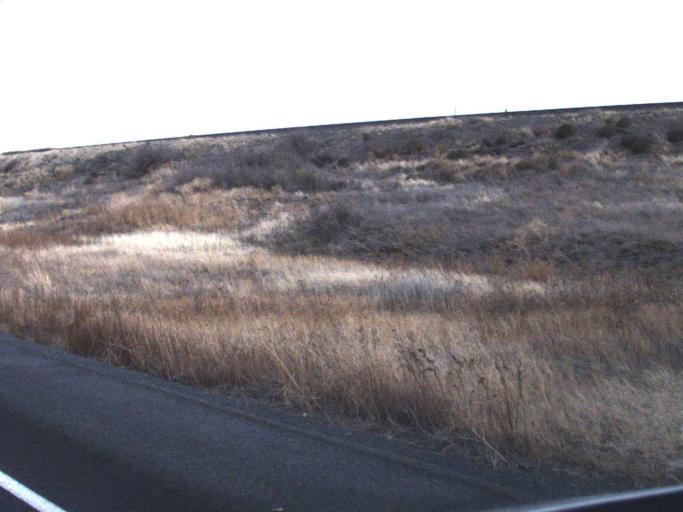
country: US
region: Washington
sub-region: Lincoln County
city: Davenport
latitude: 47.4889
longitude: -118.2508
